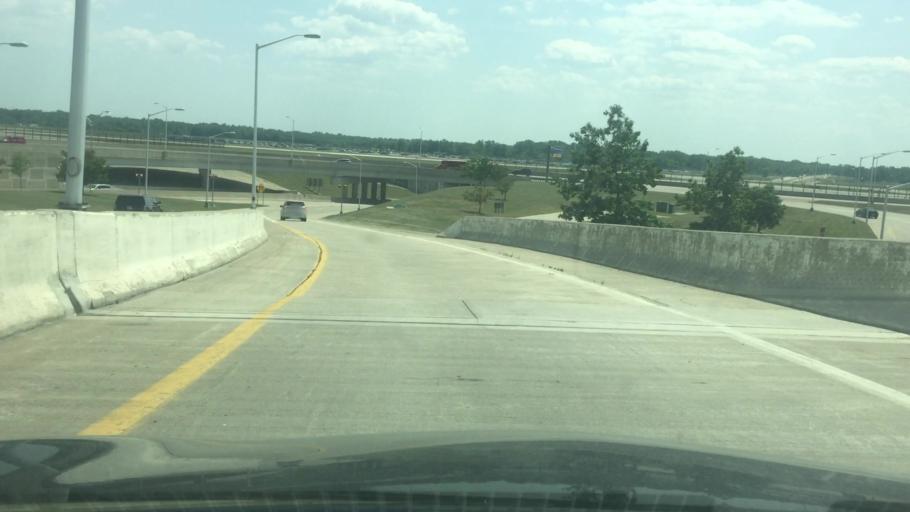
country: US
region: Michigan
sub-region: Wayne County
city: Romulus
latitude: 42.2045
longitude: -83.3580
